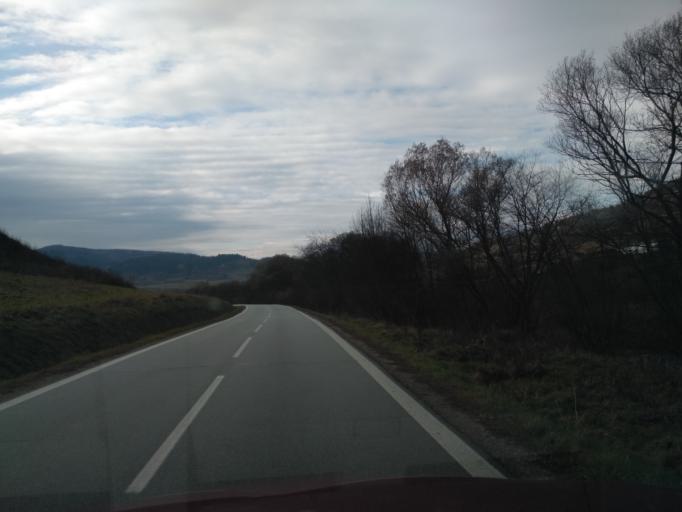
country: SK
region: Kosicky
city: Spisska Nova Ves
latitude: 48.8376
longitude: 20.6415
